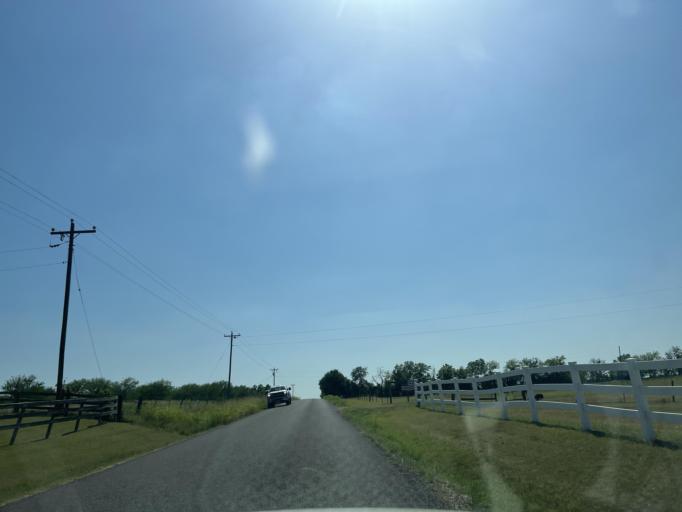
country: US
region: Texas
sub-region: Washington County
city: Brenham
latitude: 30.1587
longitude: -96.3427
